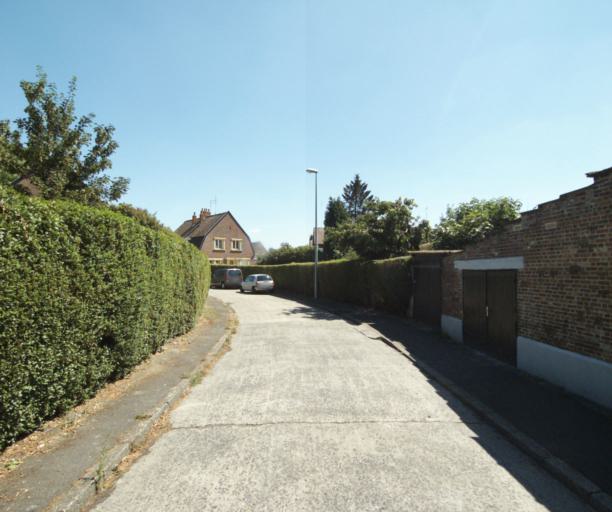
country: BE
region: Wallonia
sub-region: Province du Hainaut
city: Mouscron
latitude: 50.7392
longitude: 3.1896
